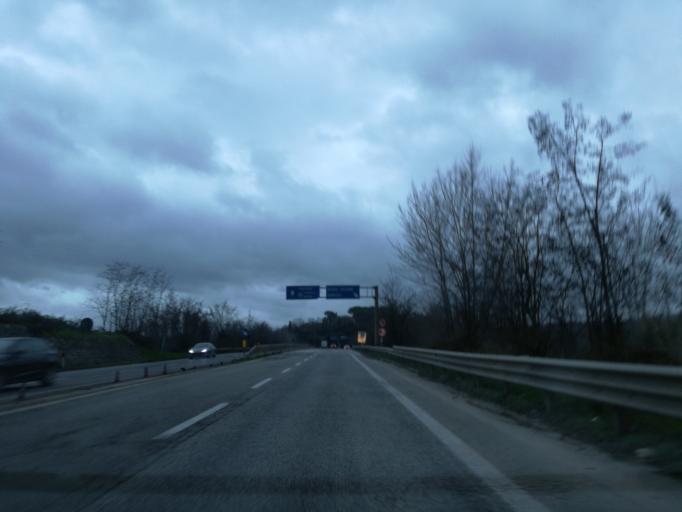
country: IT
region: Umbria
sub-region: Provincia di Perugia
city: Via Lippia
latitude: 43.0919
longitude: 12.4747
